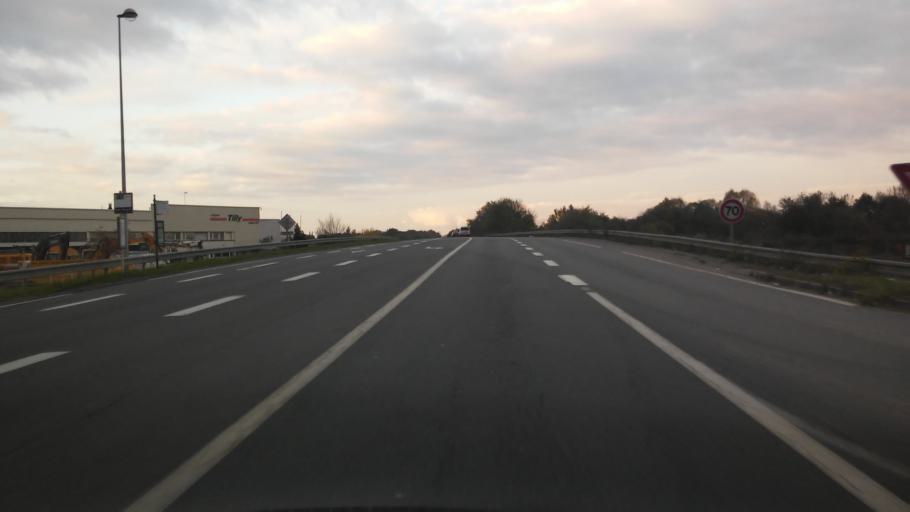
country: FR
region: Lorraine
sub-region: Departement de la Moselle
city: Woippy
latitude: 49.1596
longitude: 6.1590
